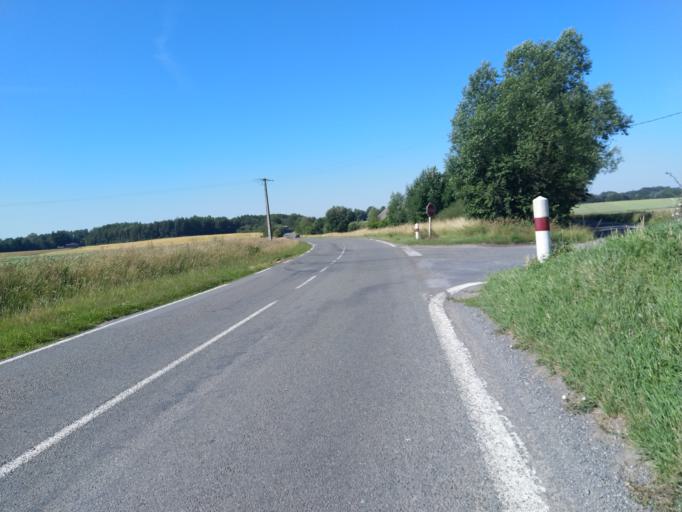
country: FR
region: Nord-Pas-de-Calais
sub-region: Departement du Nord
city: Bavay
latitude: 50.3038
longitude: 3.8195
